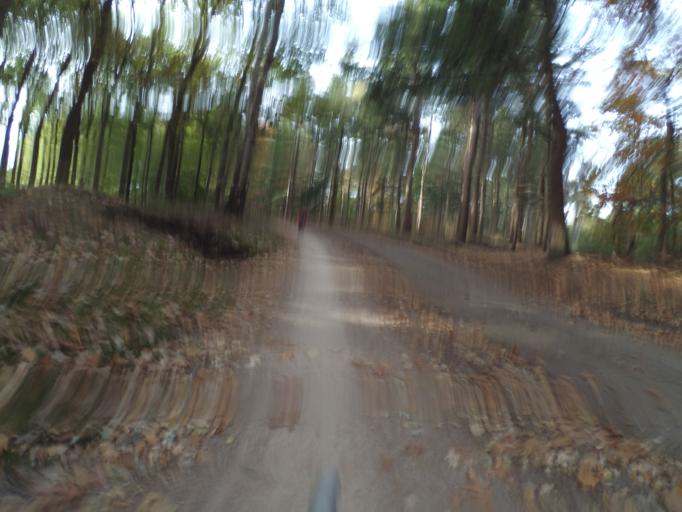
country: NL
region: Overijssel
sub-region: Gemeente Twenterand
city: Den Ham
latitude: 52.3650
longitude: 6.4266
